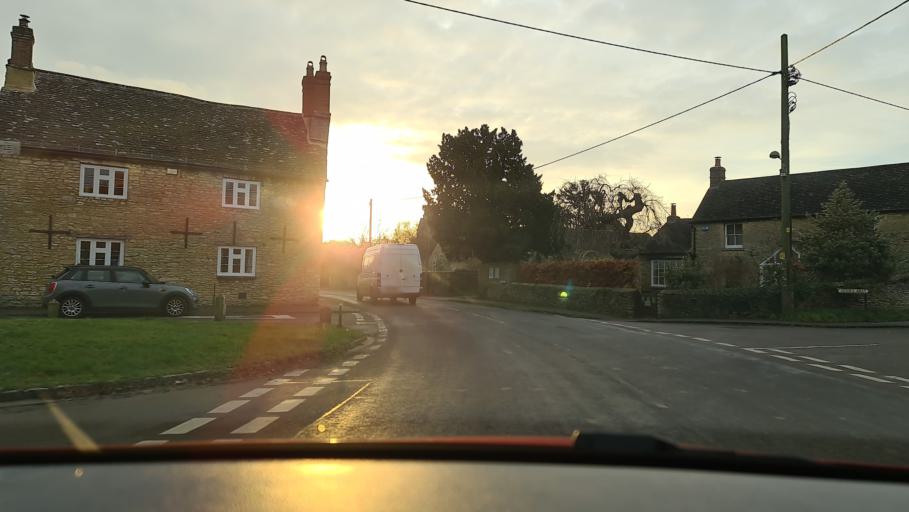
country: GB
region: England
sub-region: Oxfordshire
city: Kidlington
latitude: 51.8548
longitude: -1.2720
